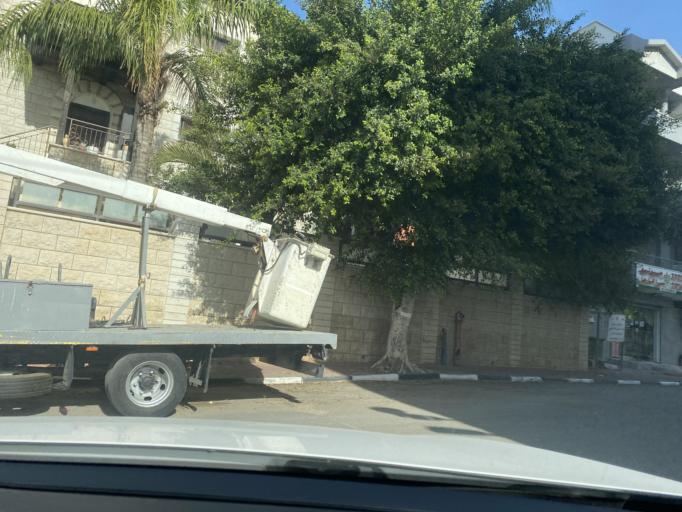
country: IL
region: Central District
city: Kafr Qasim
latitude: 32.1310
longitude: 34.9716
